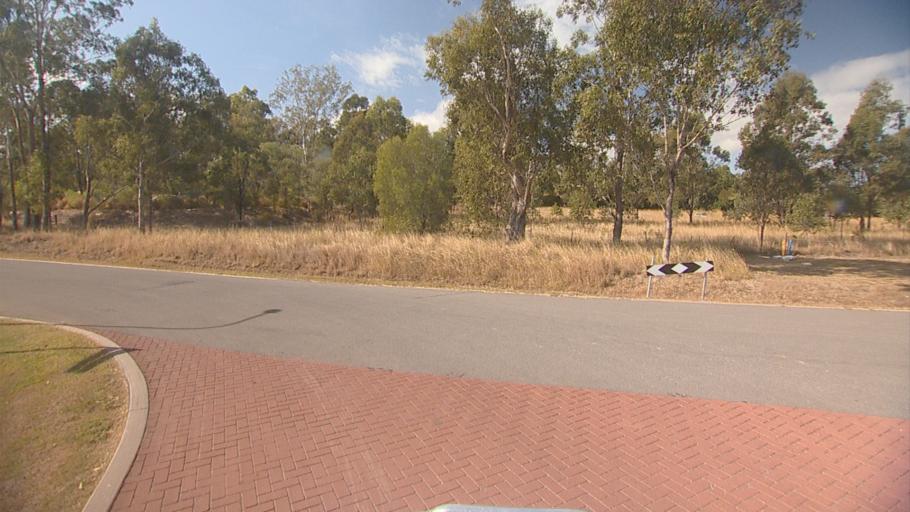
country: AU
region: Queensland
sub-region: Logan
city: Cedar Vale
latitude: -27.8742
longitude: 152.9737
